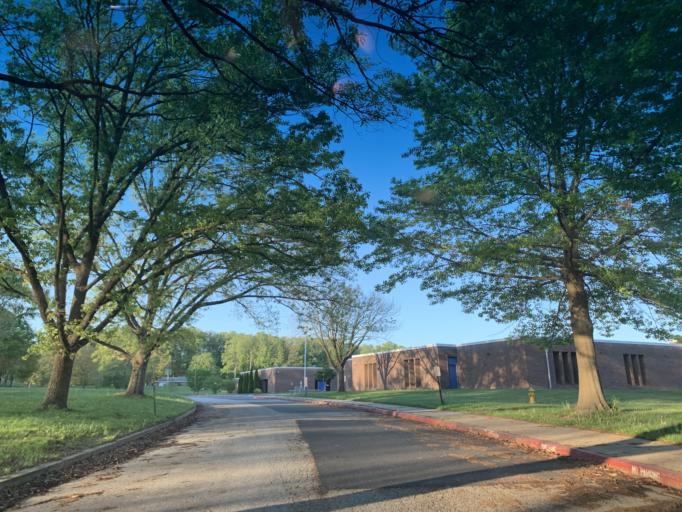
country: US
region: Maryland
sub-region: Harford County
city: Aberdeen
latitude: 39.5149
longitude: -76.1660
